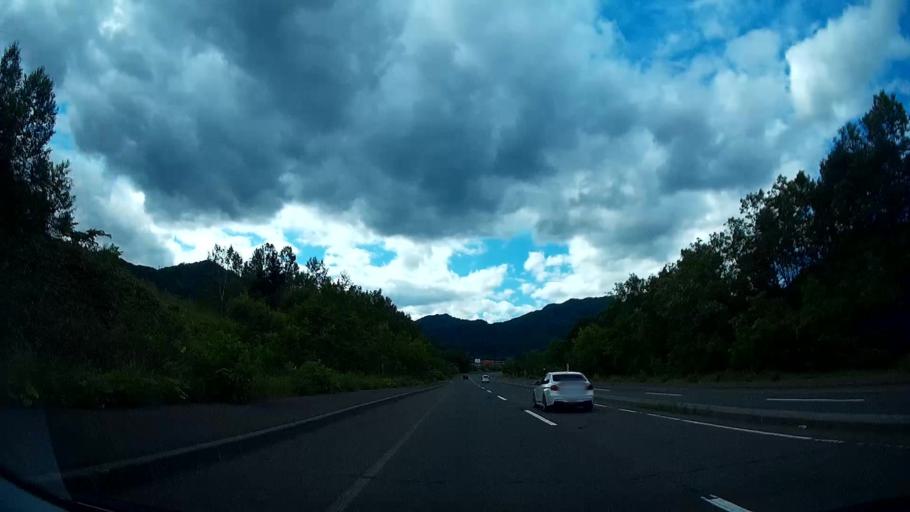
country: JP
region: Hokkaido
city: Sapporo
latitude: 42.9593
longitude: 141.2266
